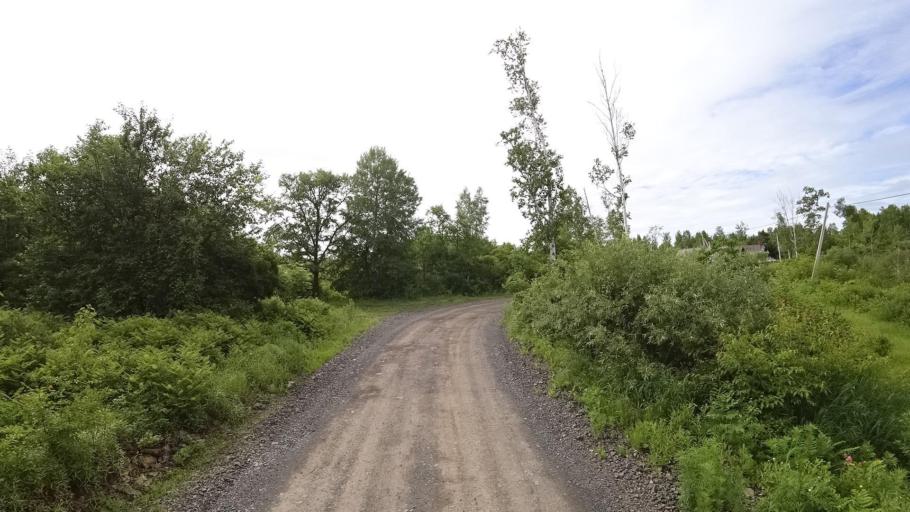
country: RU
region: Khabarovsk Krai
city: Amursk
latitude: 49.8985
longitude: 136.1491
